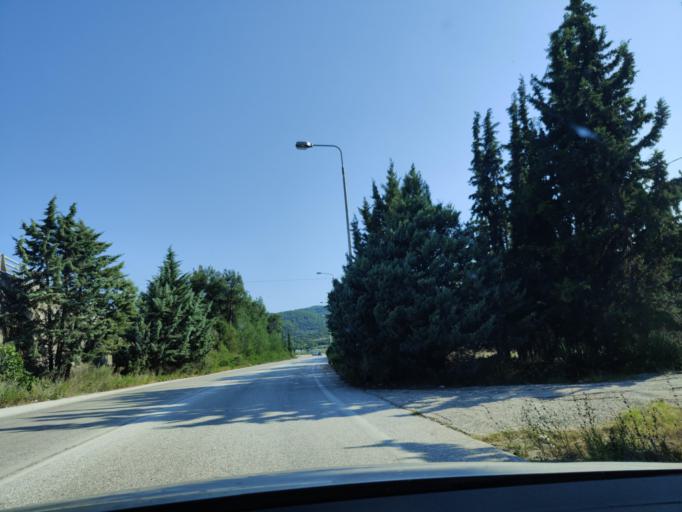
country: GR
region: East Macedonia and Thrace
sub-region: Nomos Kavalas
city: Nea Iraklitsa
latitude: 40.8678
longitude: 24.2950
